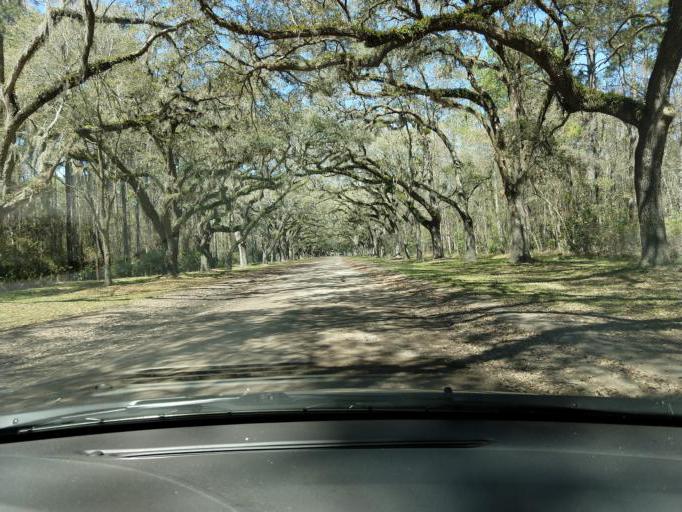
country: US
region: Georgia
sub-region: Chatham County
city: Isle of Hope
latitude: 31.9759
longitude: -81.0691
